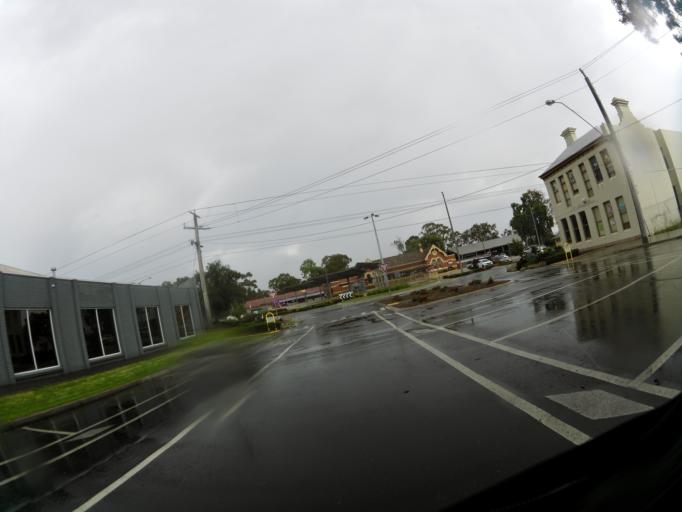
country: AU
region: Victoria
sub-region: East Gippsland
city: Bairnsdale
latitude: -37.8281
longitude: 147.6274
